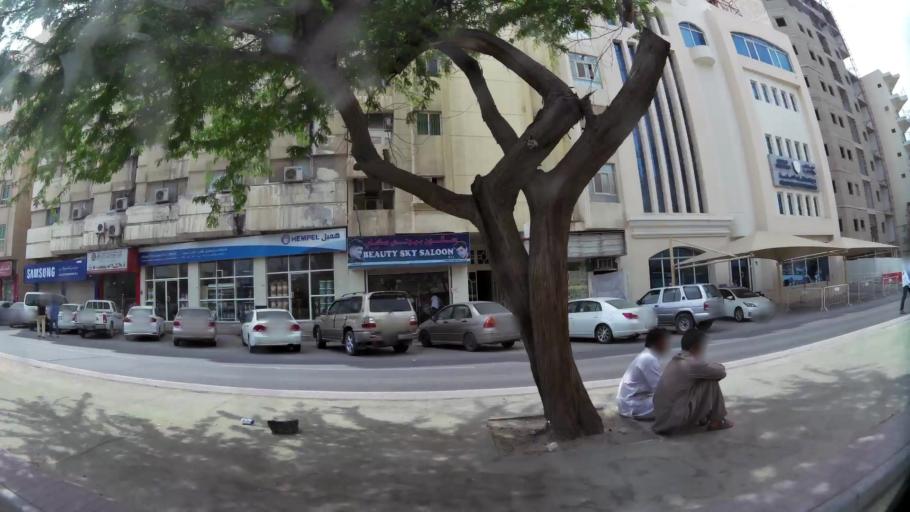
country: QA
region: Baladiyat ad Dawhah
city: Doha
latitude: 25.2857
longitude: 51.5401
